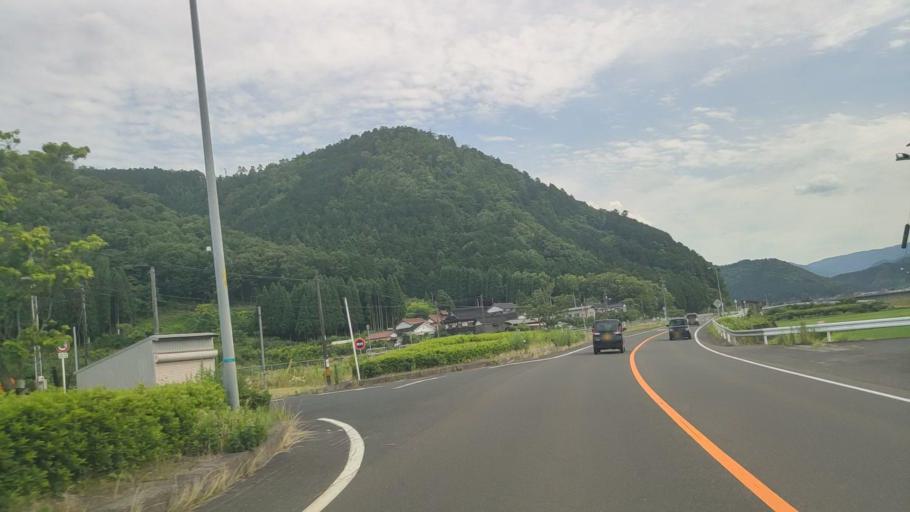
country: JP
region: Tottori
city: Tottori
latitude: 35.3687
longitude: 134.2156
